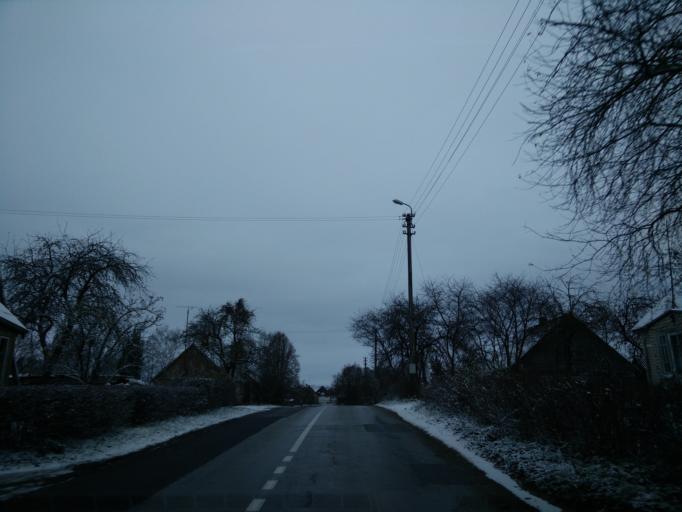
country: LT
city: Tytuveneliai
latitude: 55.4932
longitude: 23.3342
